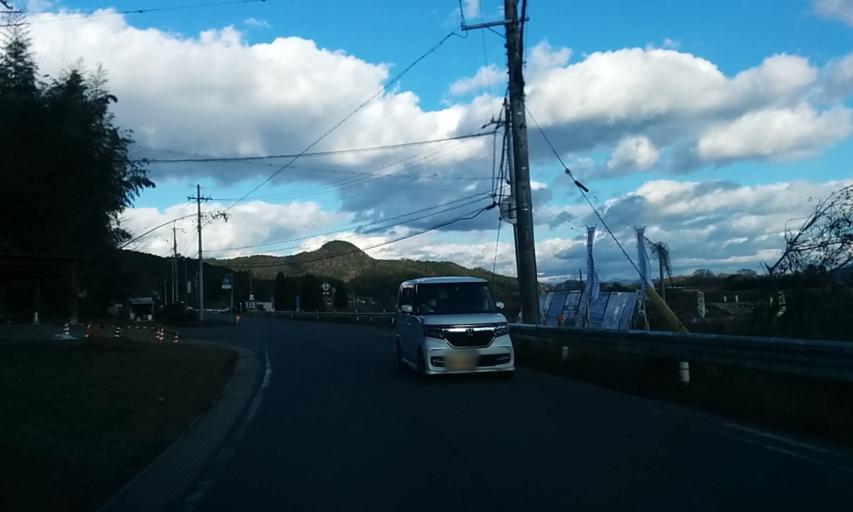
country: JP
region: Kyoto
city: Fukuchiyama
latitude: 35.3084
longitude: 135.1533
